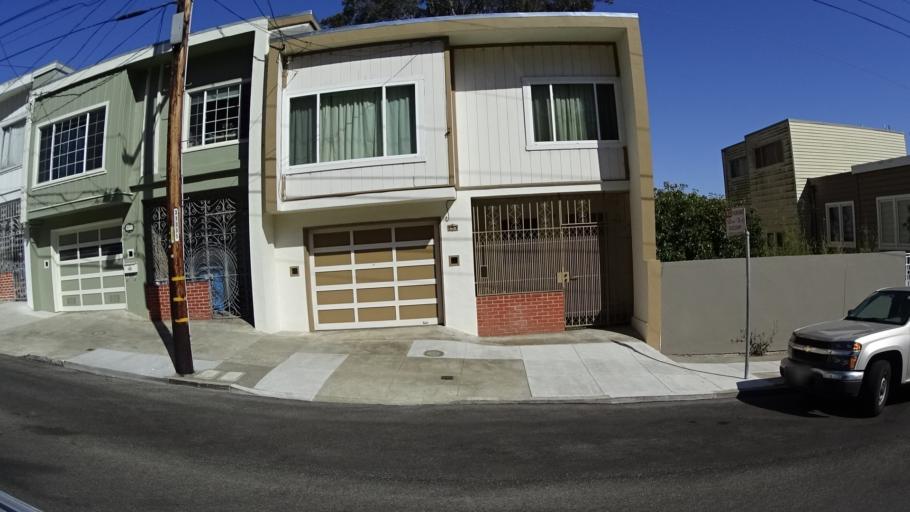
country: US
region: California
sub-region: San Mateo County
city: Daly City
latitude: 37.7240
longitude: -122.4196
